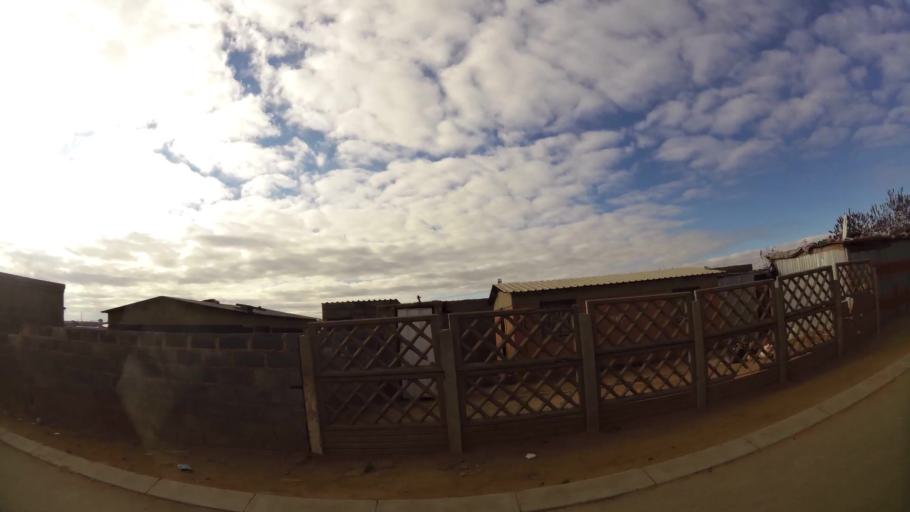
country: ZA
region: Gauteng
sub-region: City of Johannesburg Metropolitan Municipality
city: Modderfontein
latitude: -26.0387
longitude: 28.1883
